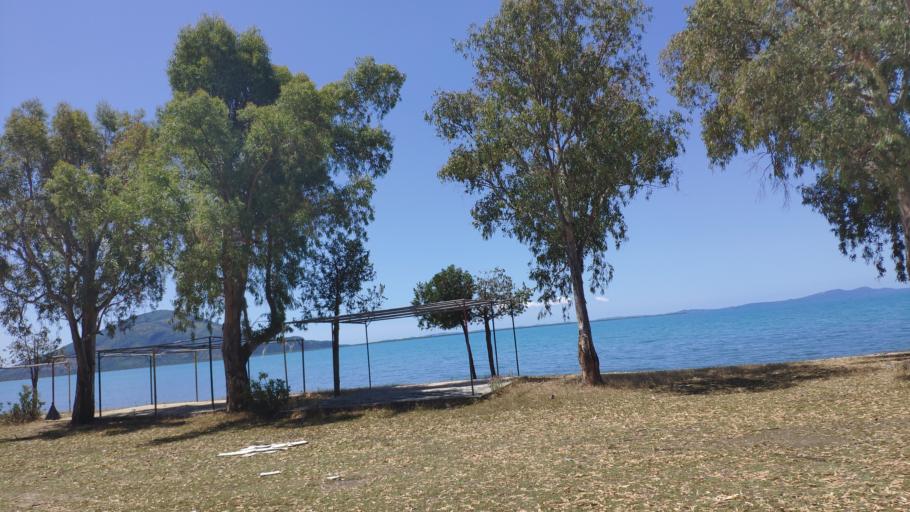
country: AL
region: Vlore
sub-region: Rrethi i Sarandes
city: Konispol
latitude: 39.6297
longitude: 20.1758
